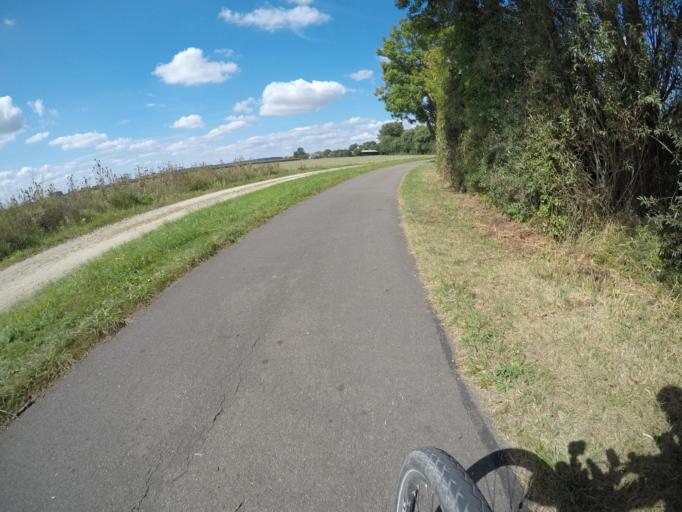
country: DE
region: Bavaria
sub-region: Swabia
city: Dillingen an der Donau
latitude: 48.6012
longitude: 10.4633
